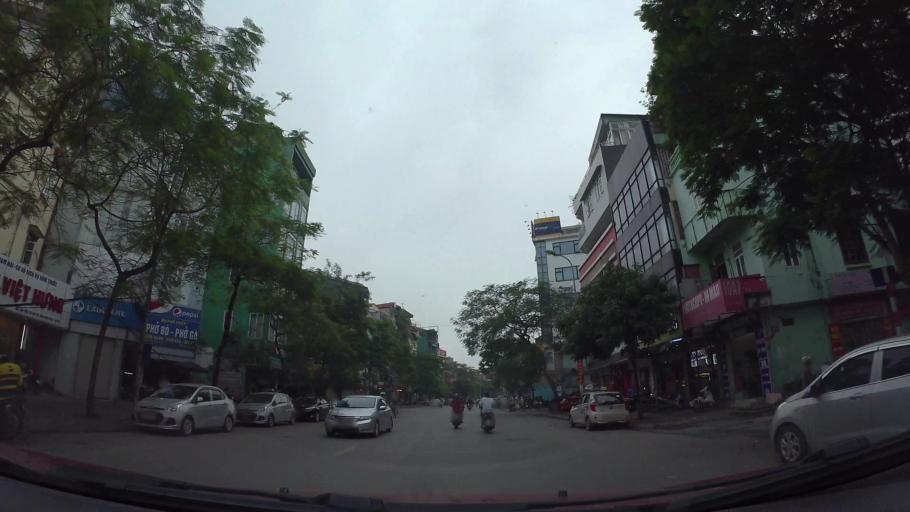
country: VN
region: Ha Noi
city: Hai BaTrung
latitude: 20.9980
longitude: 105.8458
